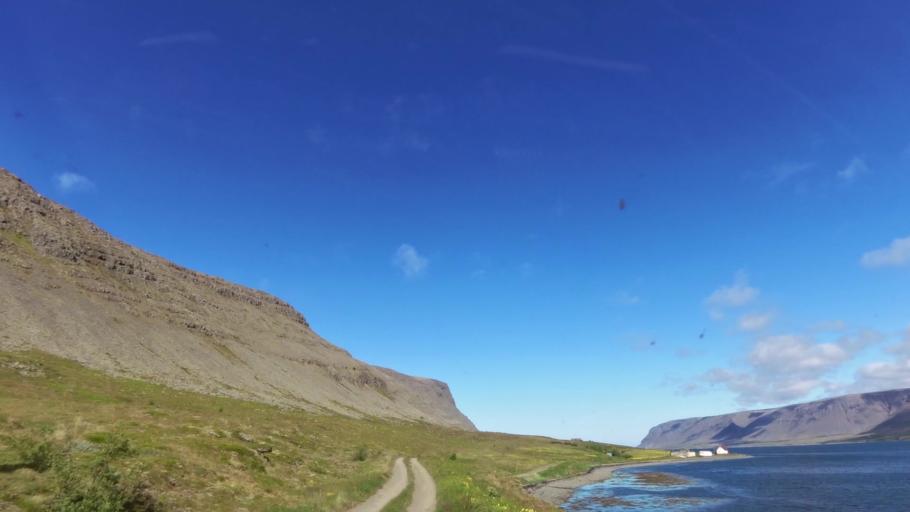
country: IS
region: West
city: Olafsvik
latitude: 65.6182
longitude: -23.8623
